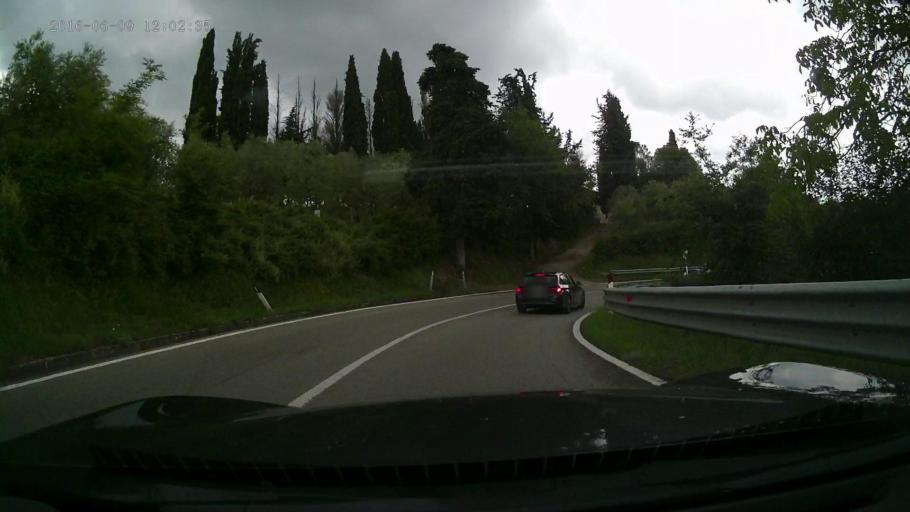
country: IT
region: Tuscany
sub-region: Province of Florence
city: Panzano in Chianti
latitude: 43.5284
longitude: 11.3039
